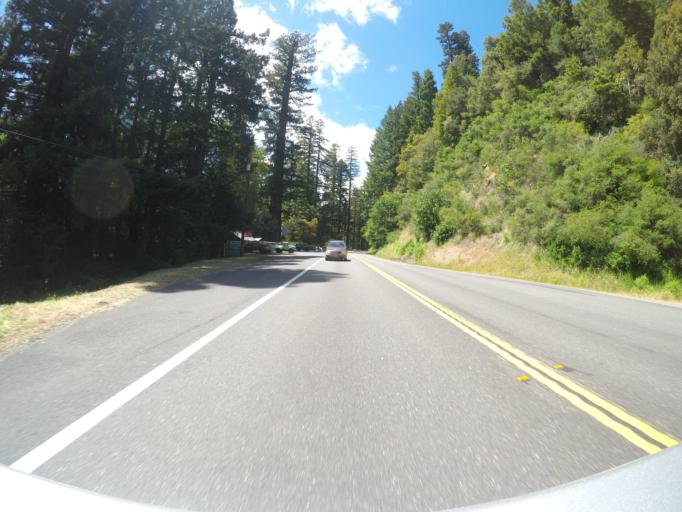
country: US
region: California
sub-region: Humboldt County
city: Redway
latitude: 39.9159
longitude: -123.7650
